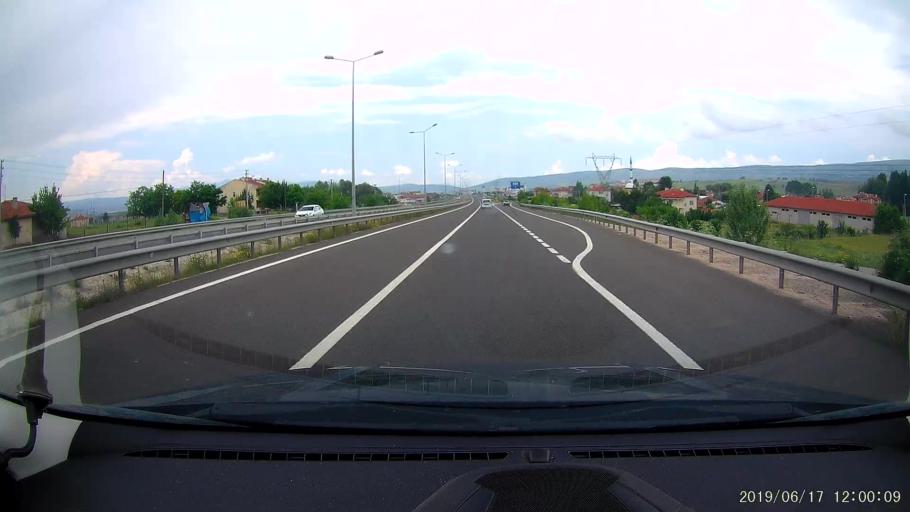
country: TR
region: Cankiri
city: Cerkes
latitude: 40.8177
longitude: 32.8985
